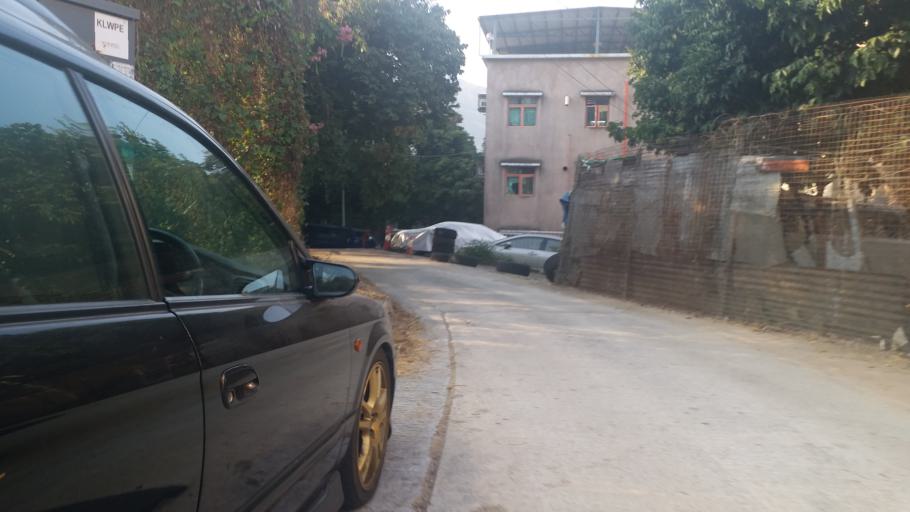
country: HK
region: Tuen Mun
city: Tuen Mun
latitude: 22.4115
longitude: 113.9747
